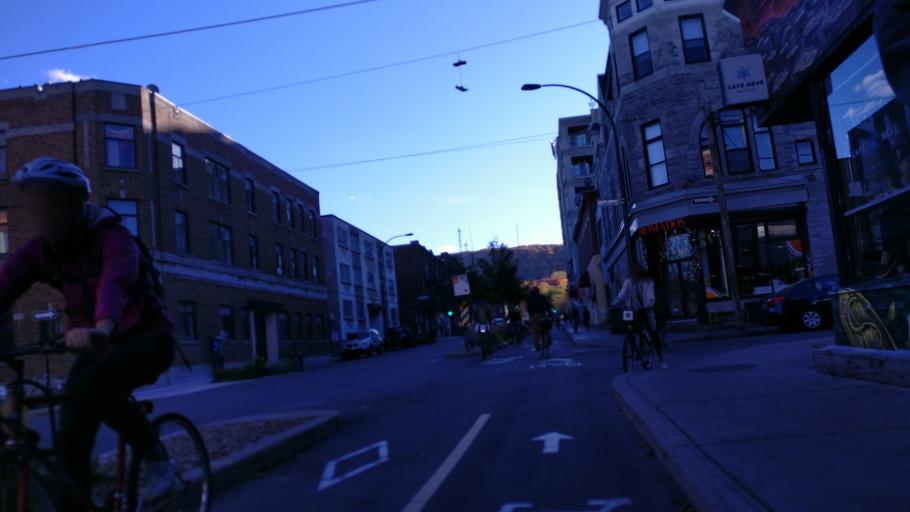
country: CA
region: Quebec
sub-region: Montreal
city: Montreal
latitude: 45.5195
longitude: -73.5803
